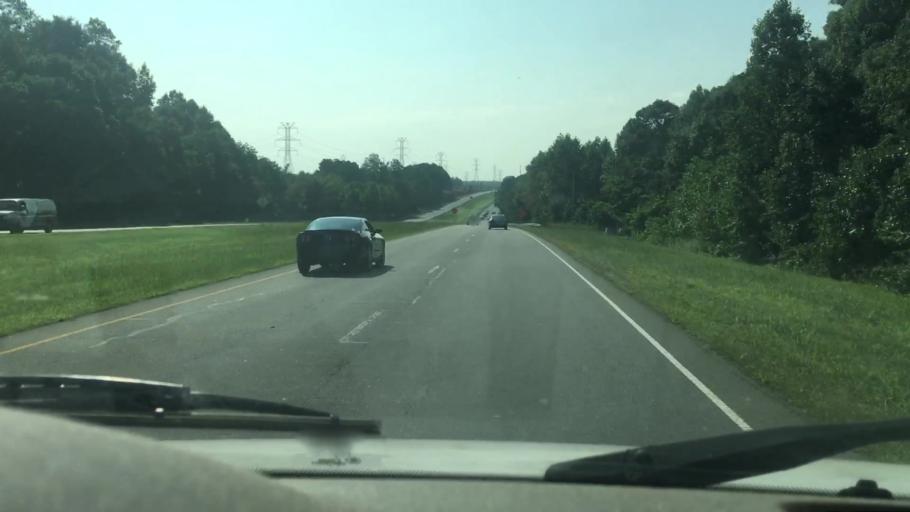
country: US
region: North Carolina
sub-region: Gaston County
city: Mount Holly
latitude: 35.3312
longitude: -80.9534
